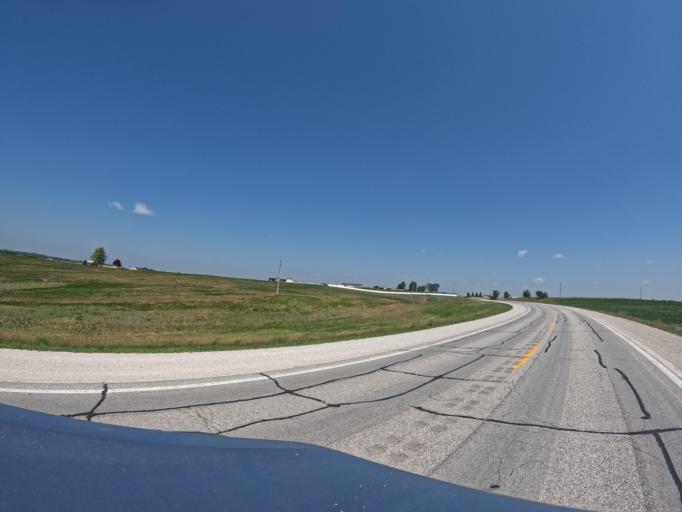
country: US
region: Iowa
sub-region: Keokuk County
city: Sigourney
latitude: 41.2486
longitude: -92.2051
